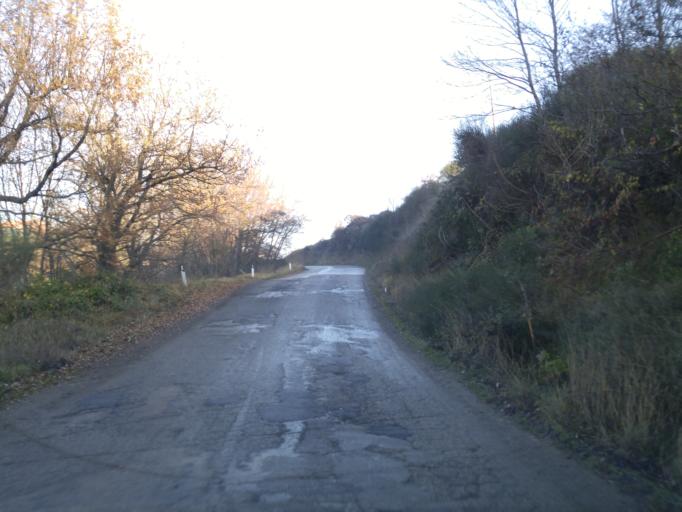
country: IT
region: The Marches
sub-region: Provincia di Pesaro e Urbino
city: Mombaroccio
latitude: 43.7759
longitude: 12.8326
